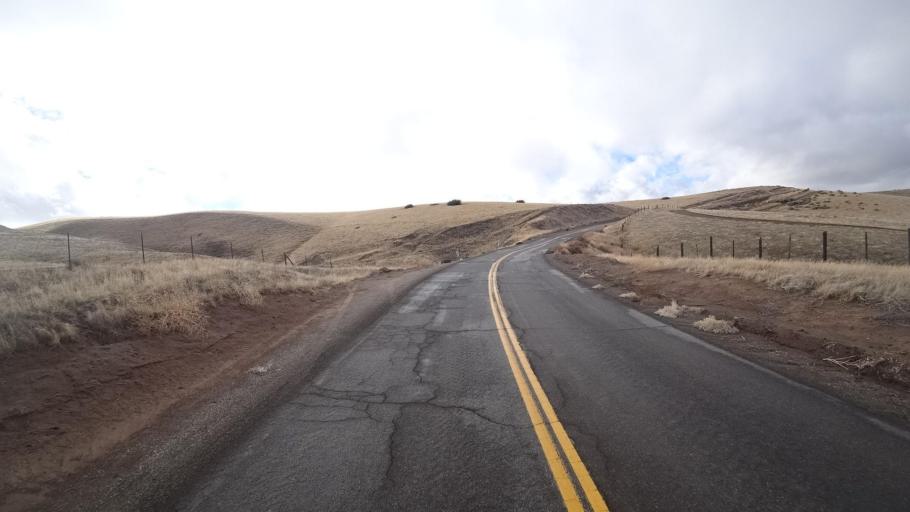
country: US
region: California
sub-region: Kern County
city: Maricopa
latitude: 34.9218
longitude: -119.4096
